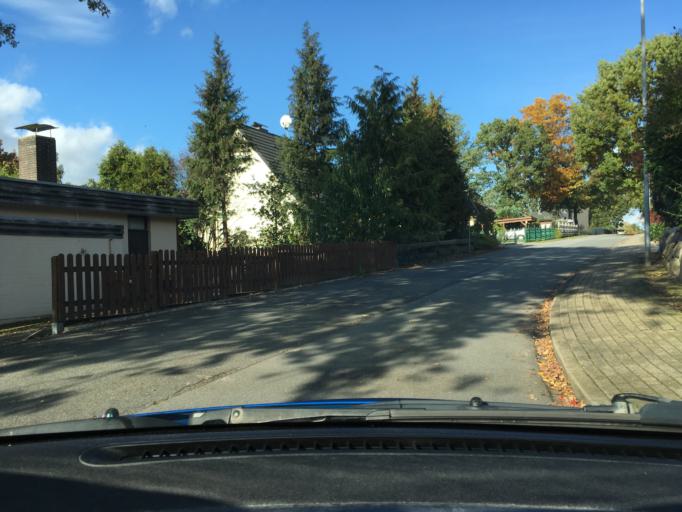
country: DE
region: Lower Saxony
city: Kakenstorf
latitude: 53.3102
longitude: 9.7876
